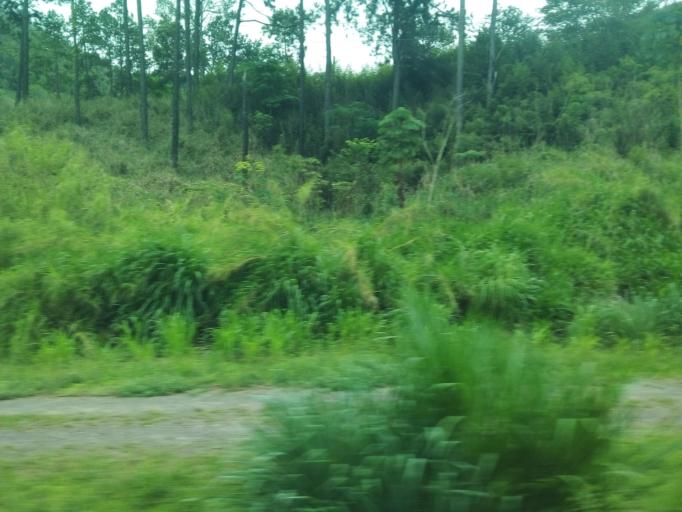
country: BR
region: Minas Gerais
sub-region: Nova Era
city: Nova Era
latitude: -19.7272
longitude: -43.0104
